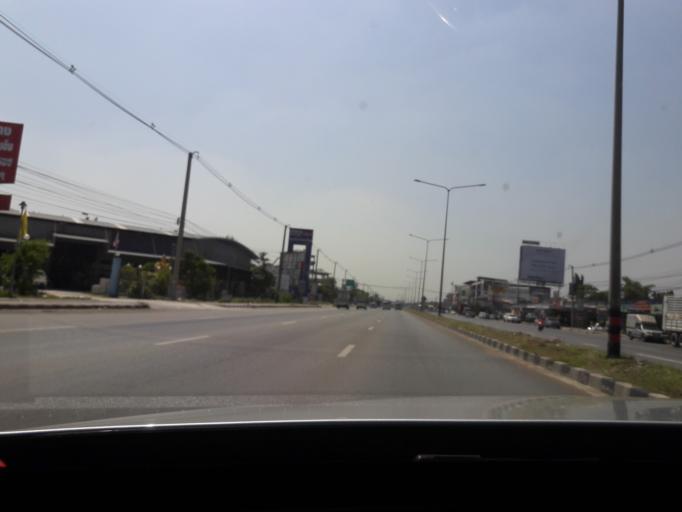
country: TH
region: Samut Sakhon
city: Krathum Baen
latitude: 13.6571
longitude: 100.3093
